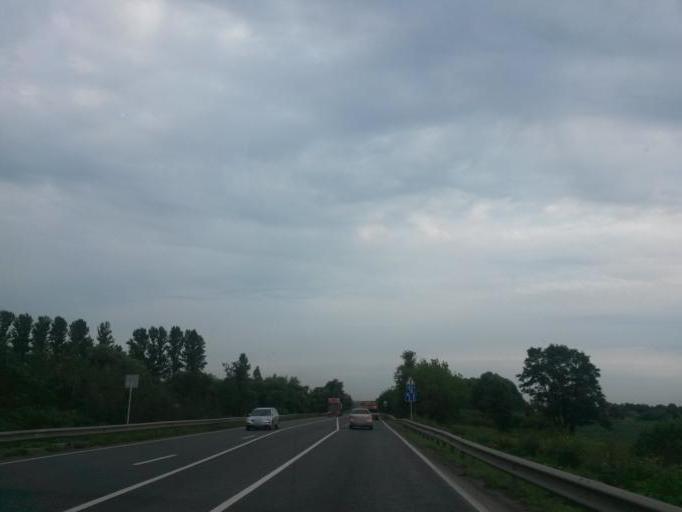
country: RU
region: Moskovskaya
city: Yam
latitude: 55.4974
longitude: 37.7502
